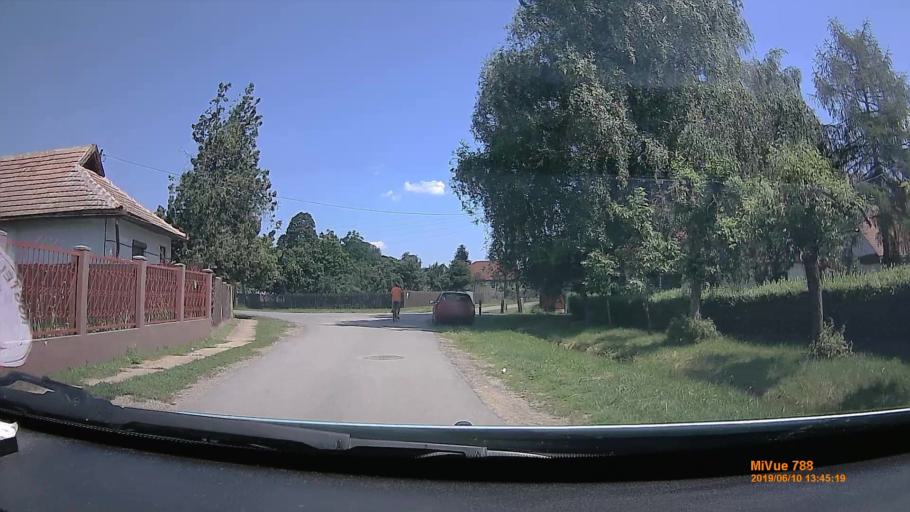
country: HU
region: Szabolcs-Szatmar-Bereg
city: Tiszadob
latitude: 48.0094
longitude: 21.1682
